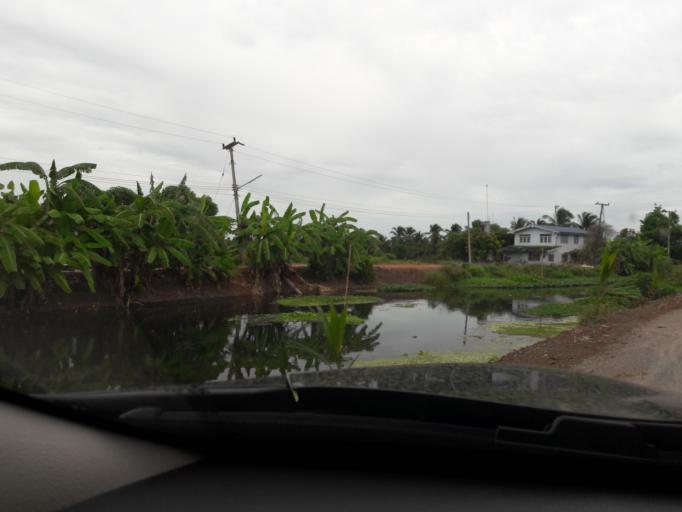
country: TH
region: Ratchaburi
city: Bang Phae
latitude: 13.6117
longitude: 99.9650
